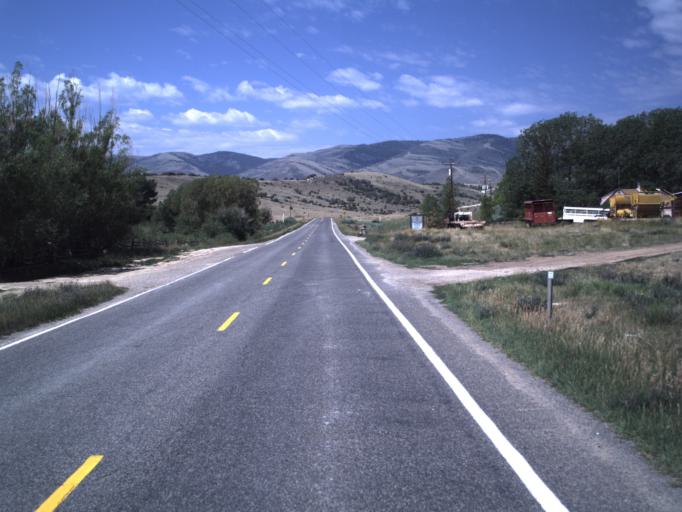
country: US
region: Utah
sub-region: Daggett County
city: Manila
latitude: 40.9770
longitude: -109.8215
